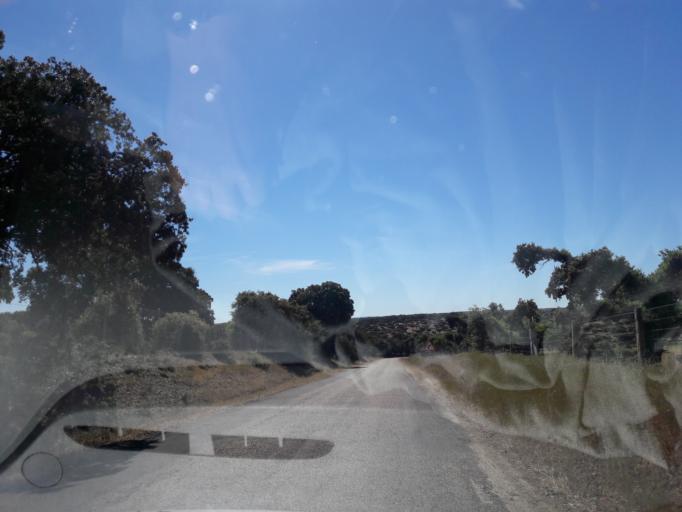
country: ES
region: Castille and Leon
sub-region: Provincia de Salamanca
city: Vega de Tirados
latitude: 41.0617
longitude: -5.8952
